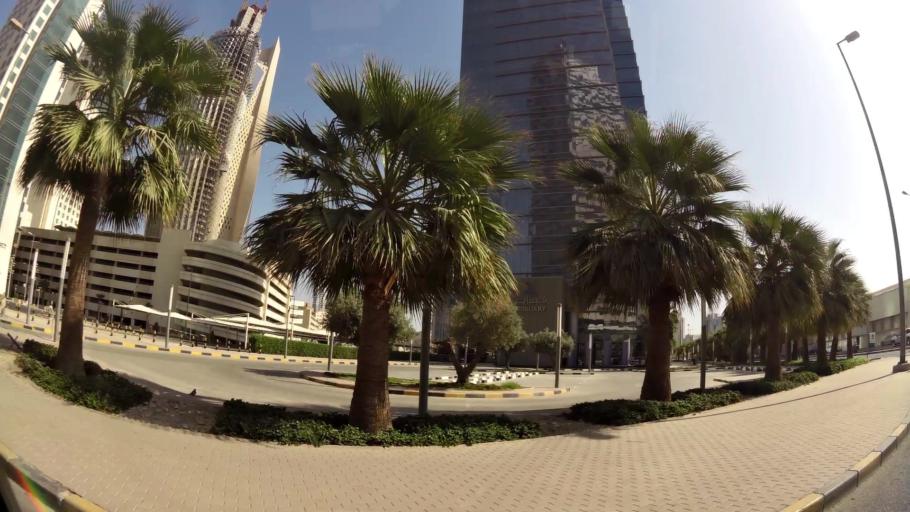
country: KW
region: Al Asimah
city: Kuwait City
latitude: 29.3752
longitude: 47.9905
